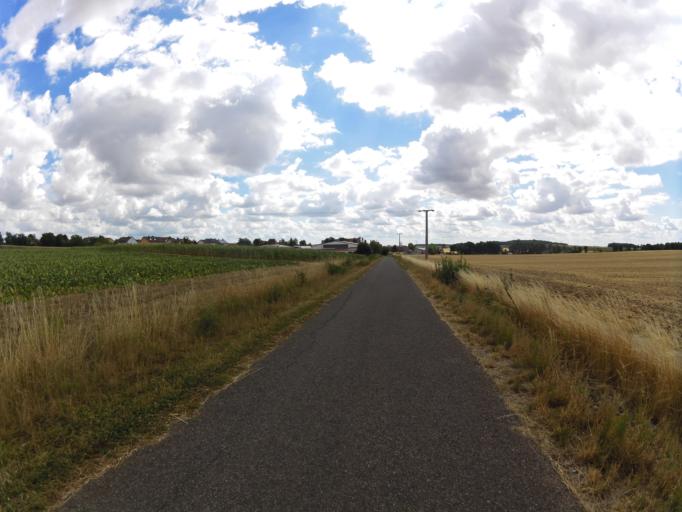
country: DE
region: Bavaria
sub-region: Regierungsbezirk Unterfranken
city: Sonderhofen
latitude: 49.5761
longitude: 10.0112
